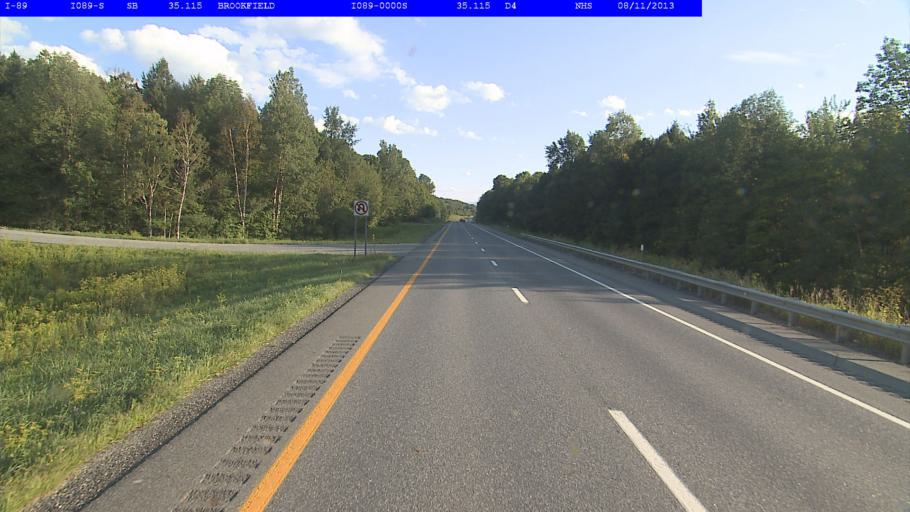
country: US
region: Vermont
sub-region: Orange County
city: Randolph
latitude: 44.0054
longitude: -72.6219
